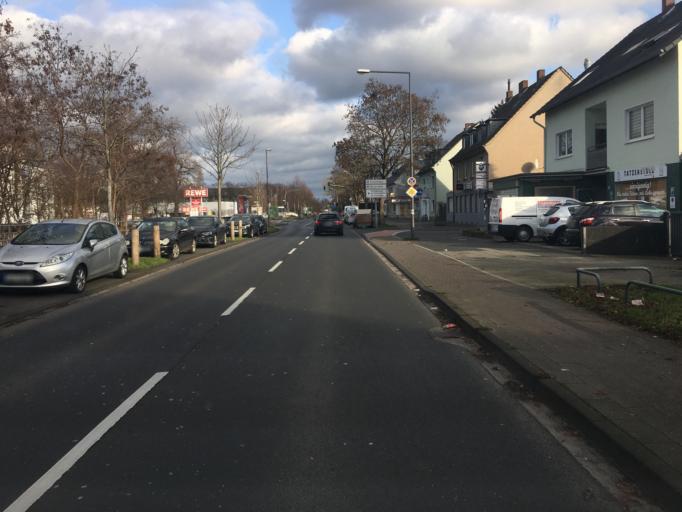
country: DE
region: North Rhine-Westphalia
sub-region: Regierungsbezirk Koln
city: Muelheim
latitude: 50.9809
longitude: 7.0235
